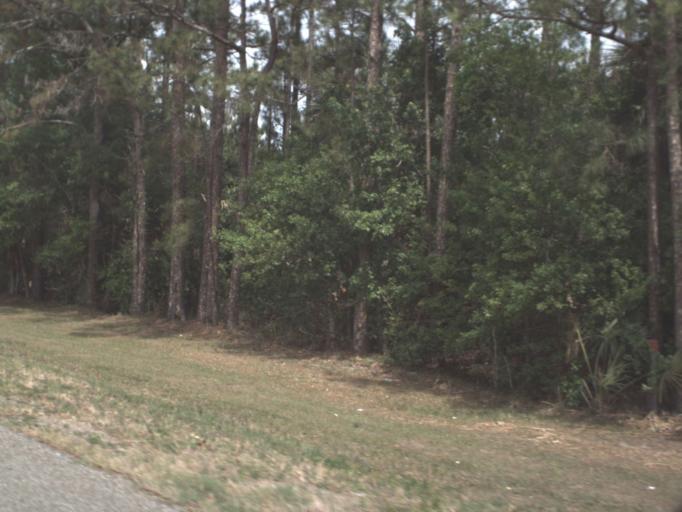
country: US
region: Florida
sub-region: Flagler County
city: Bunnell
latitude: 29.3187
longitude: -81.3107
